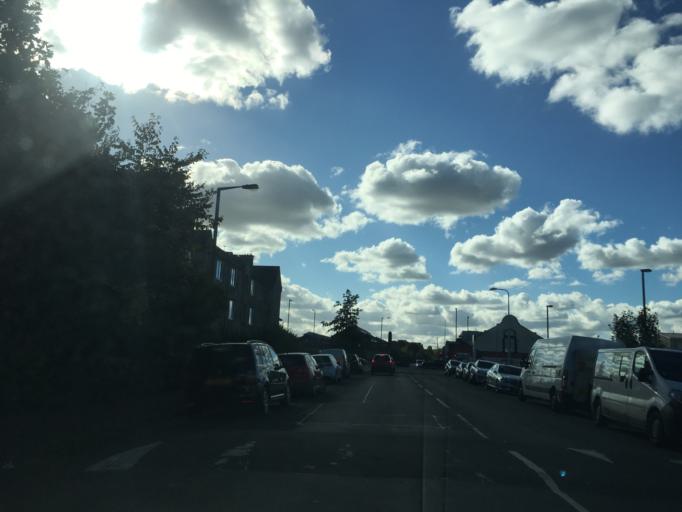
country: GB
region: Scotland
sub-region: Edinburgh
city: Colinton
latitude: 55.9290
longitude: -3.2457
